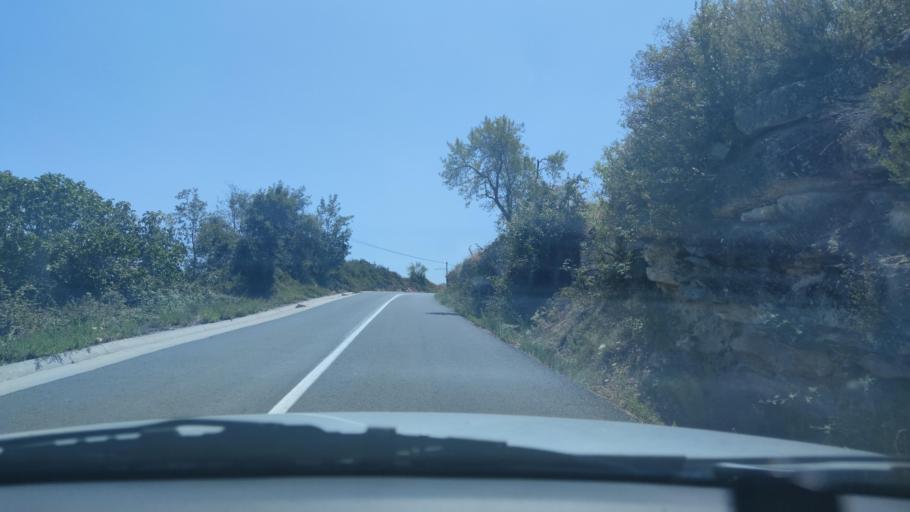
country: ES
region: Catalonia
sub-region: Provincia de Lleida
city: Vinaixa
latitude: 41.4205
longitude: 0.9538
